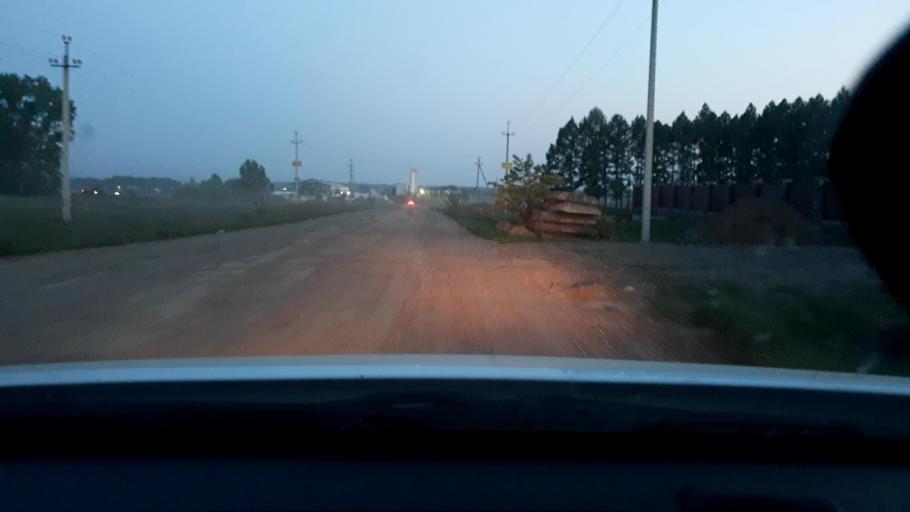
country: RU
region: Bashkortostan
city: Avdon
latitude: 54.5142
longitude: 55.8220
